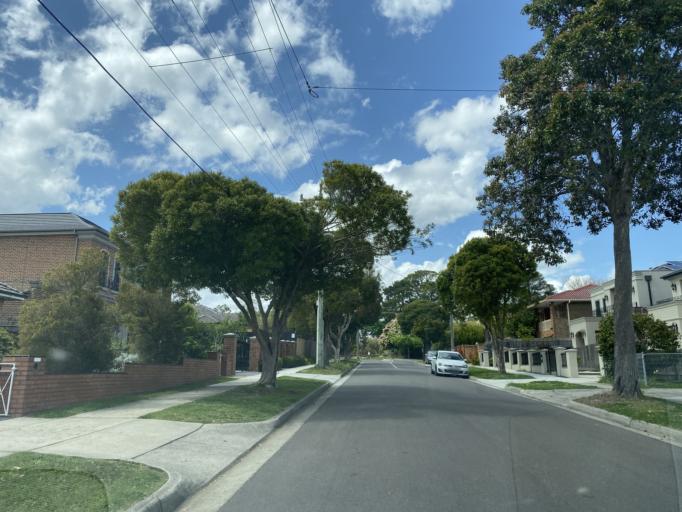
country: AU
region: Victoria
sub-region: Whitehorse
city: Burwood
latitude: -37.8606
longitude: 145.1209
